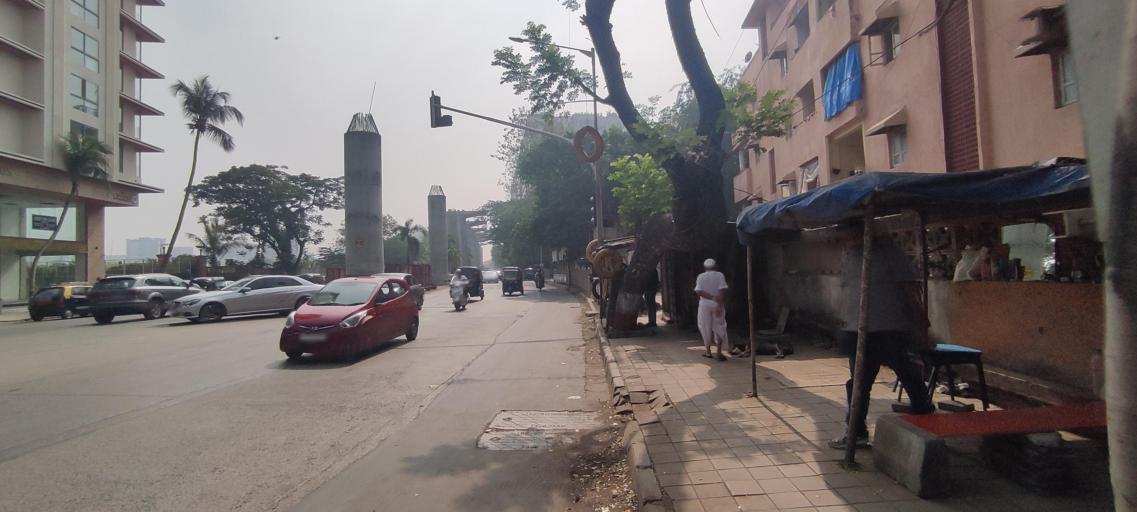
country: IN
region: Maharashtra
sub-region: Mumbai Suburban
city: Mumbai
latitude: 19.1217
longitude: 72.8298
